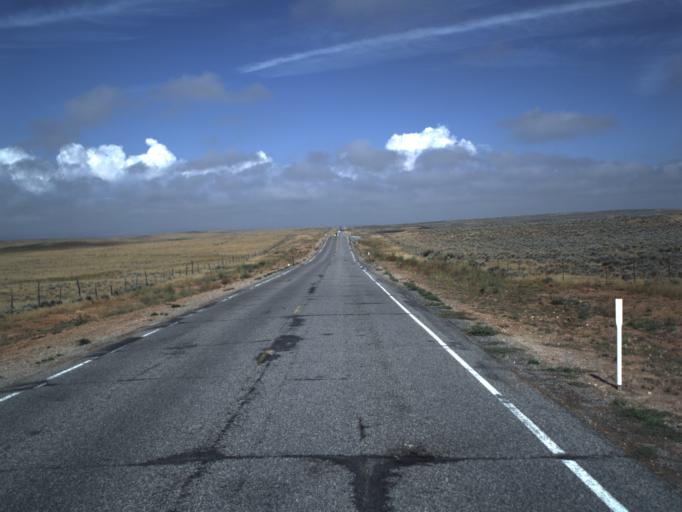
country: US
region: Wyoming
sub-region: Uinta County
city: Evanston
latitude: 41.4271
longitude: -111.0559
